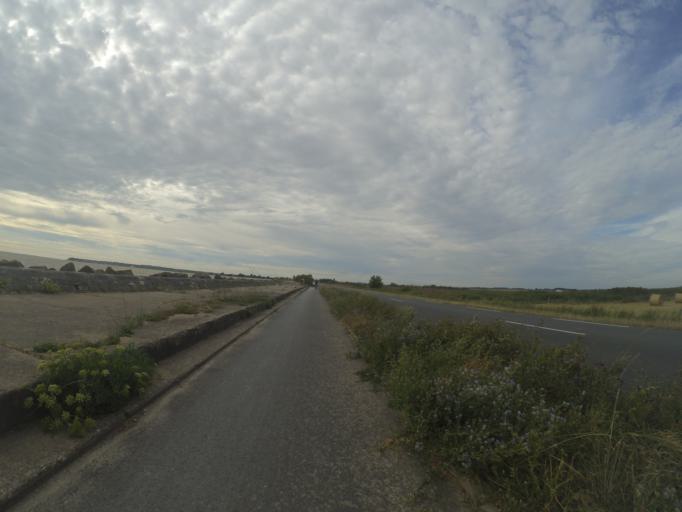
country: FR
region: Poitou-Charentes
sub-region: Departement de la Charente-Maritime
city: Meschers-sur-Gironde
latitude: 45.5447
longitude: -0.9107
